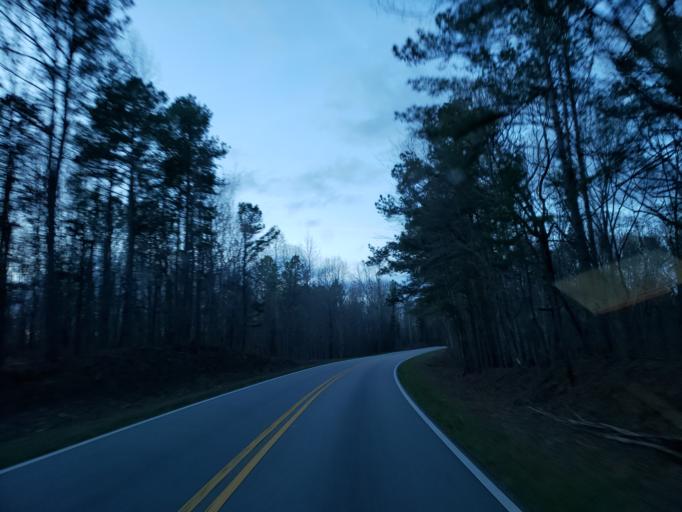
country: US
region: Georgia
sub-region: Paulding County
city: Dallas
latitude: 33.9972
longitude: -84.9248
